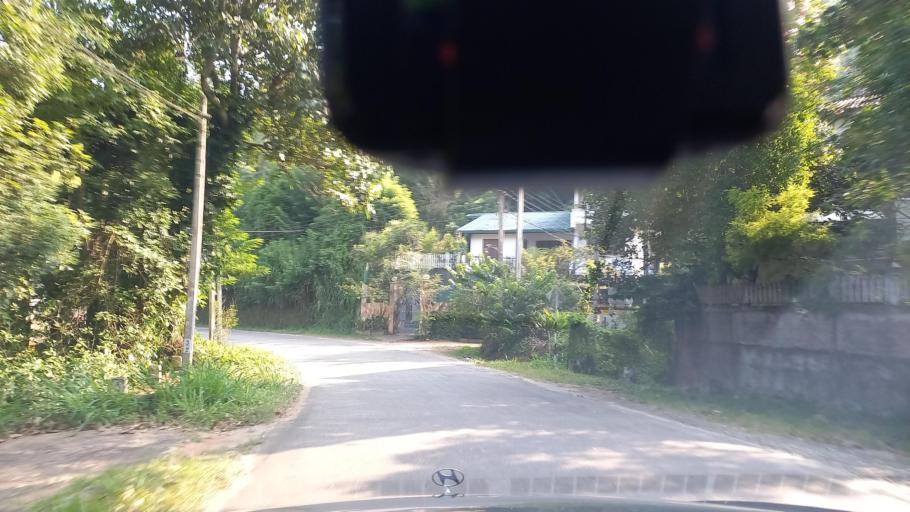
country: LK
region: Central
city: Gampola
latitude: 7.2220
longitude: 80.6058
